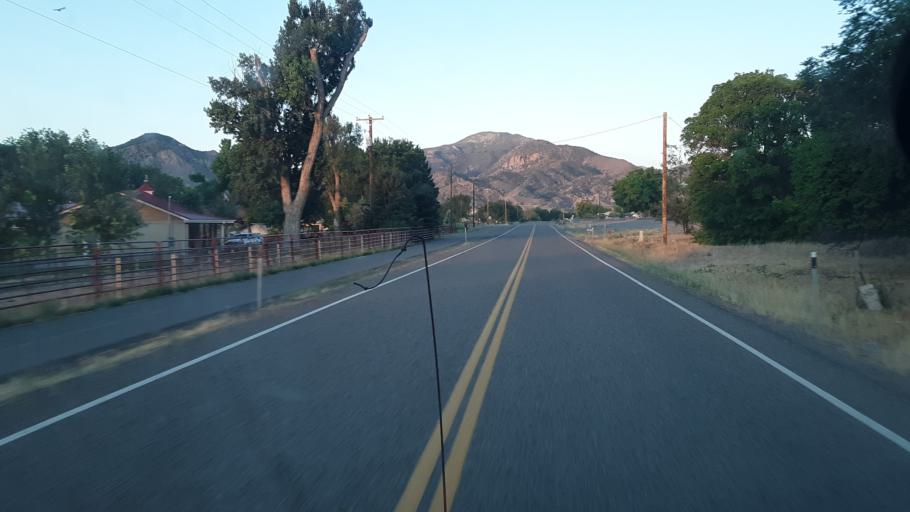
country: US
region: Utah
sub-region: Sevier County
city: Monroe
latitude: 38.5967
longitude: -112.2483
